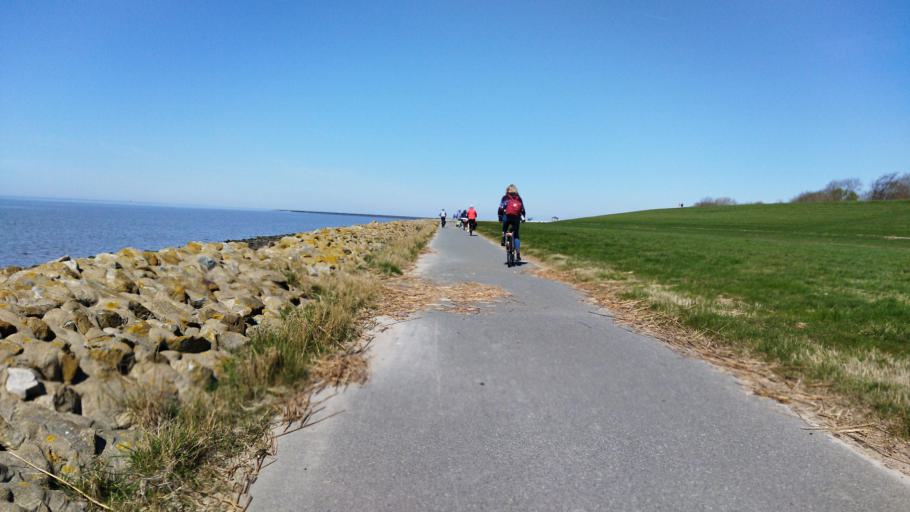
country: DE
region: Lower Saxony
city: Wremen
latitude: 53.6261
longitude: 8.5063
